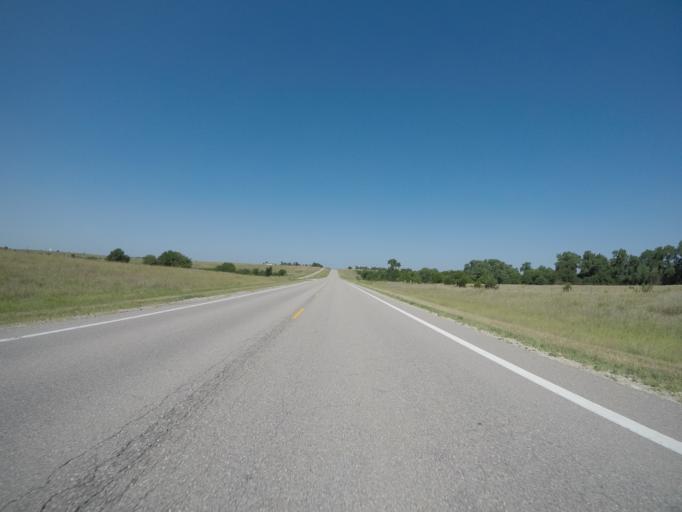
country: US
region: Kansas
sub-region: Clay County
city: Clay Center
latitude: 39.3648
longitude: -97.4297
